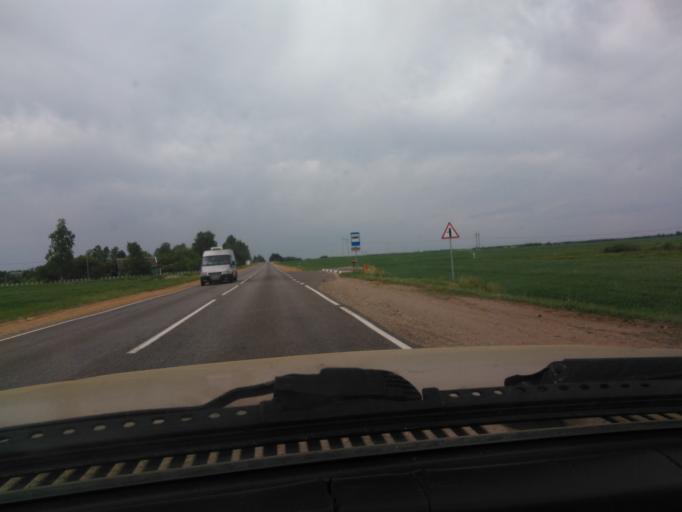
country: BY
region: Mogilev
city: Kamyennyya Lavy
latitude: 54.0534
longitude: 30.3263
